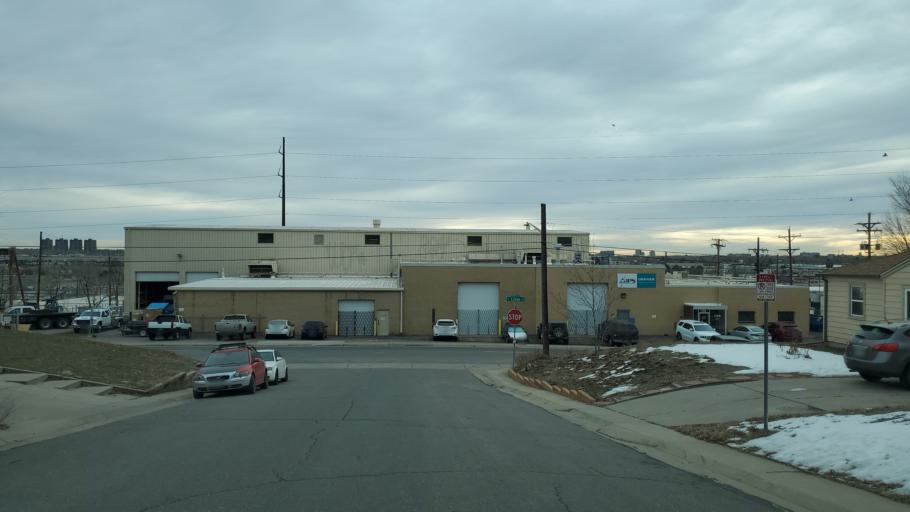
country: US
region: Colorado
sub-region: Denver County
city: Denver
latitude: 39.6981
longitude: -105.0021
